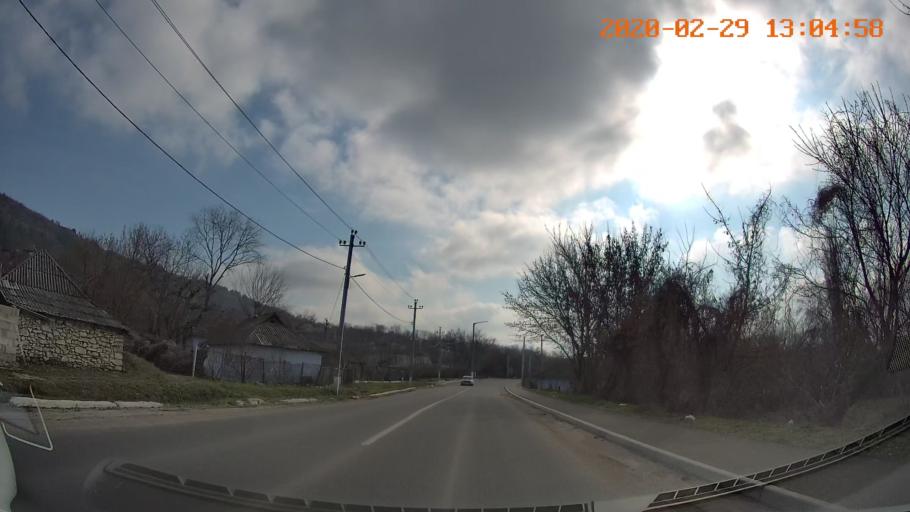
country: MD
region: Telenesti
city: Camenca
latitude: 48.0238
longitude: 28.7080
